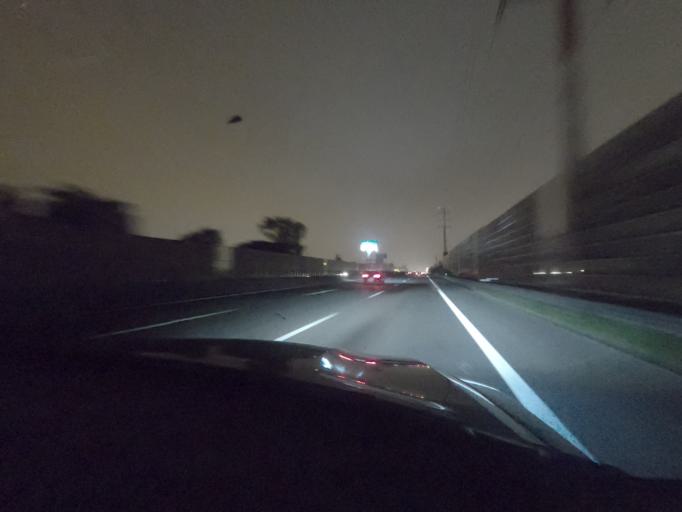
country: PT
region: Lisbon
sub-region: Loures
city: Sao Joao da Talha
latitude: 38.8291
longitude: -9.0978
